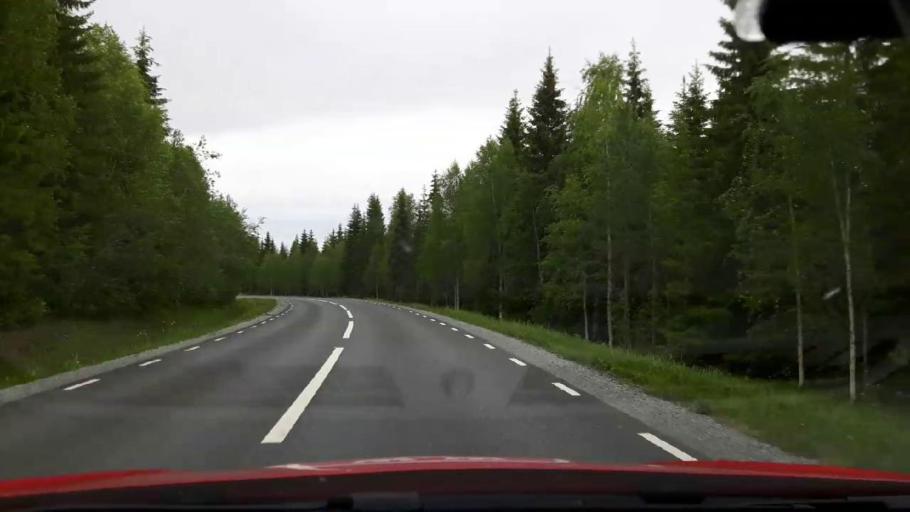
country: SE
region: Jaemtland
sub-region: OEstersunds Kommun
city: Lit
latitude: 63.7430
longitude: 14.8097
